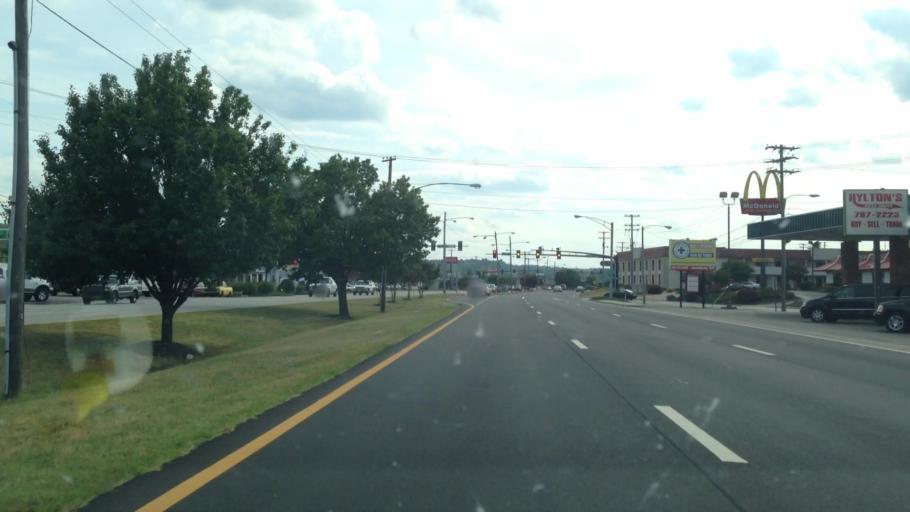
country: US
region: Virginia
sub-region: City of Danville
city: Danville
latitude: 36.5881
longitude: -79.4214
